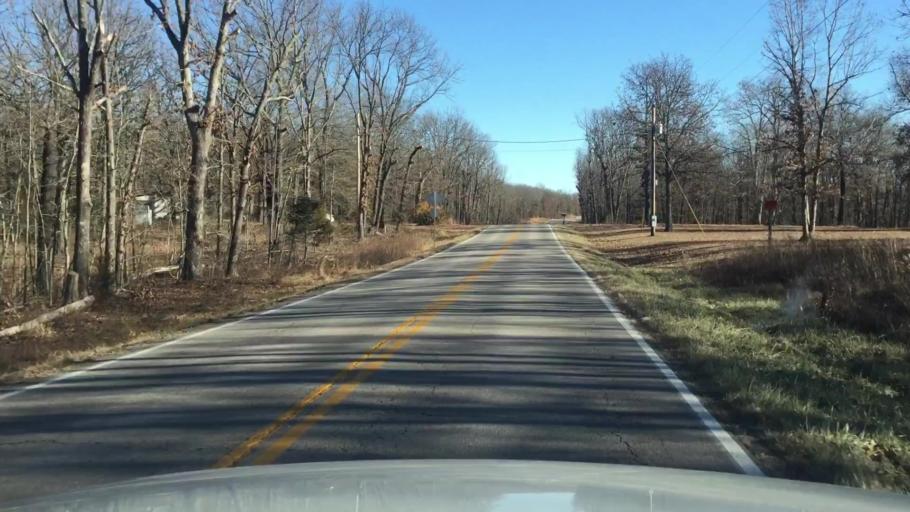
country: US
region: Missouri
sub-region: Morgan County
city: Versailles
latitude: 38.3488
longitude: -92.7461
